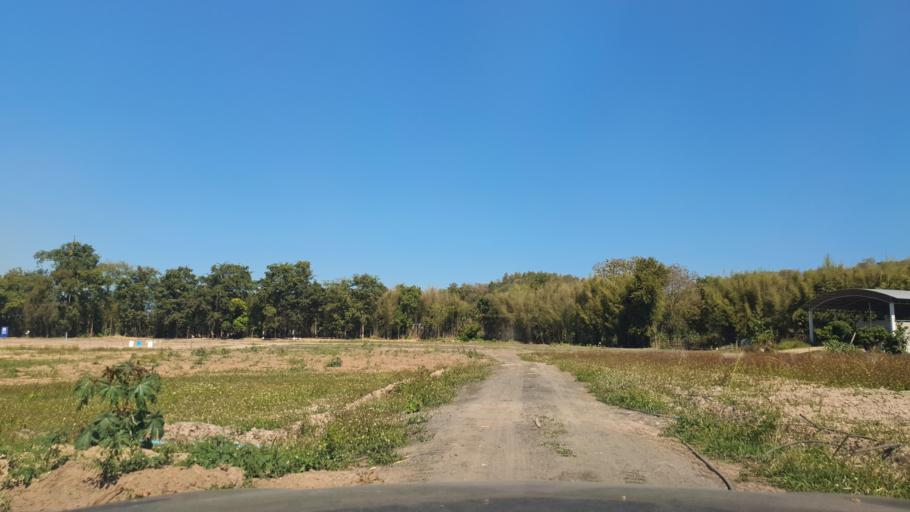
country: TH
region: Chiang Mai
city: Mae Wang
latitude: 18.6833
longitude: 98.8124
